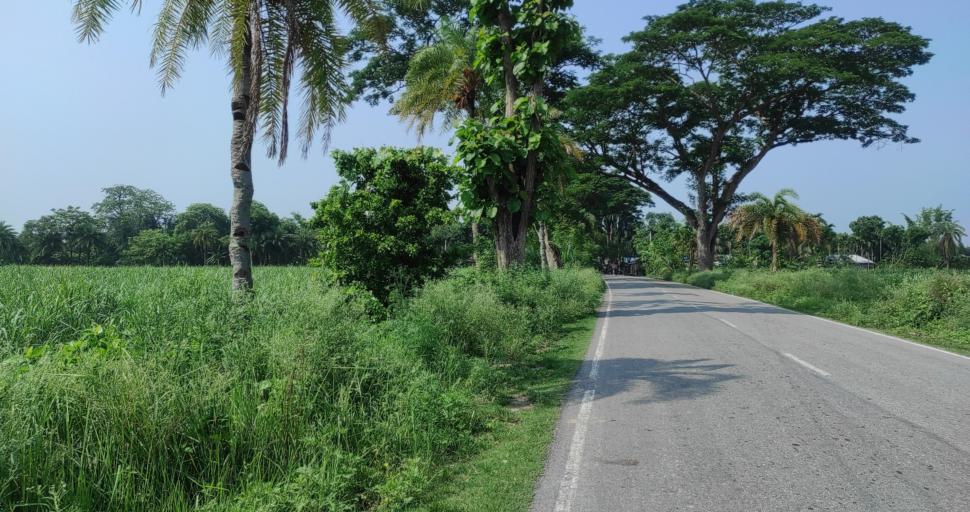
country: BD
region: Rajshahi
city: Ishurdi
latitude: 24.2630
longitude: 89.0498
